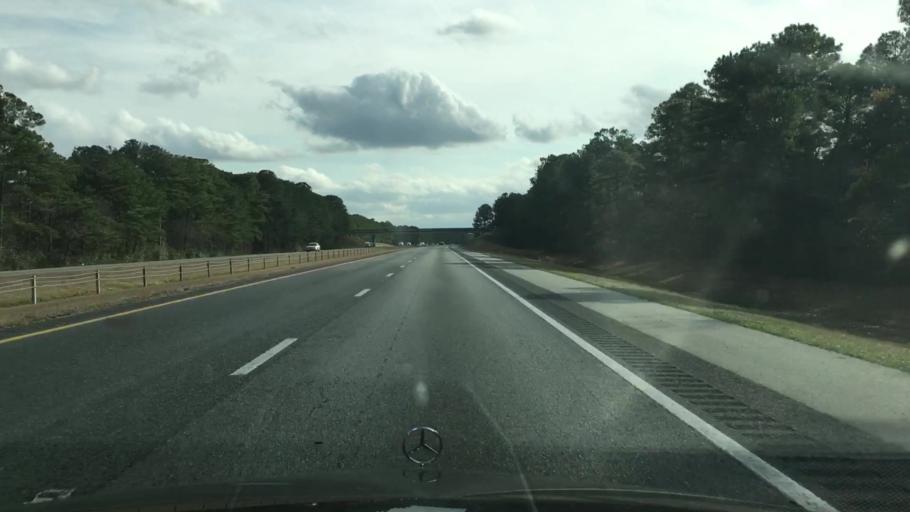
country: US
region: North Carolina
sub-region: Duplin County
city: Warsaw
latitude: 35.0528
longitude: -78.1562
